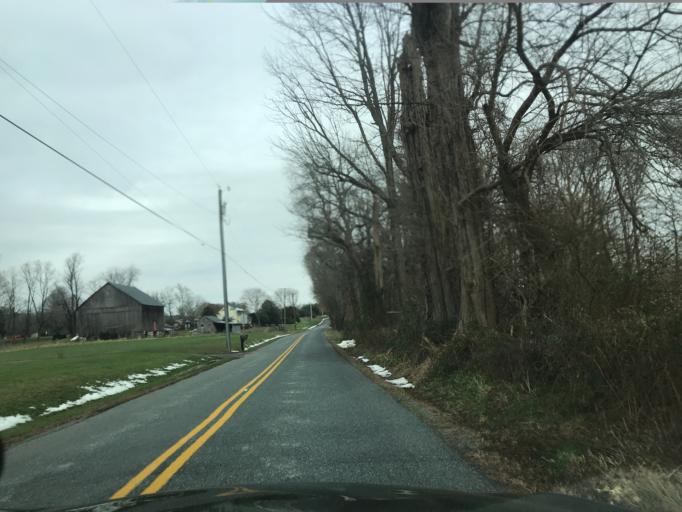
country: US
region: Maryland
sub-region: Harford County
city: Jarrettsville
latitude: 39.6730
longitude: -76.4308
